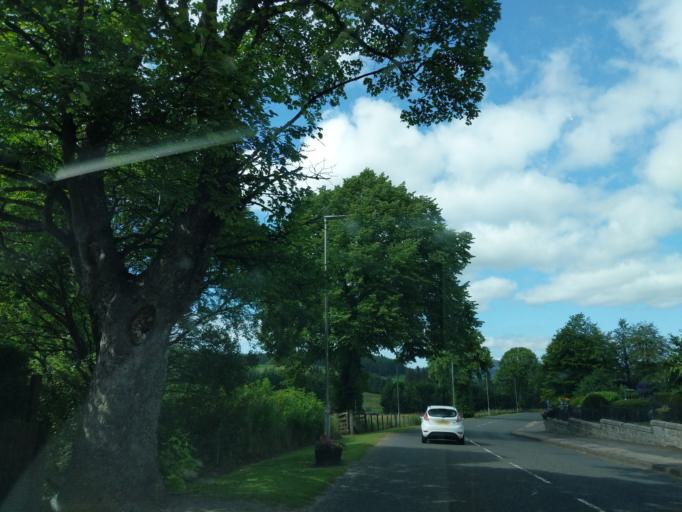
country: GB
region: Scotland
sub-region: Moray
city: Dufftown
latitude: 57.4496
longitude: -3.1308
